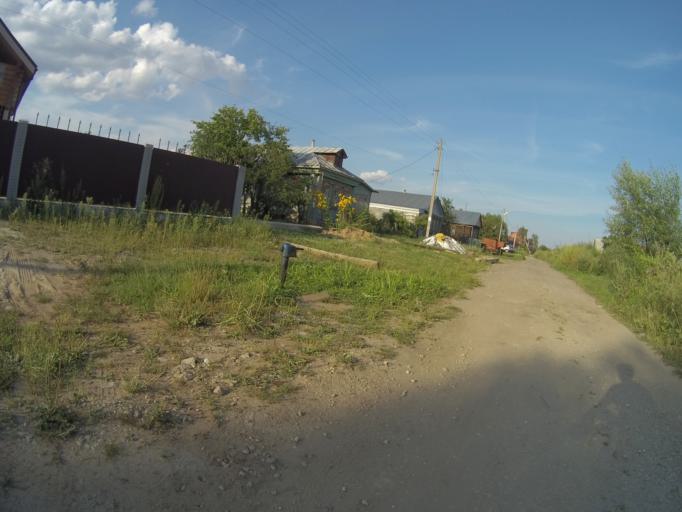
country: RU
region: Vladimir
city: Raduzhnyy
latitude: 56.0216
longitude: 40.3341
